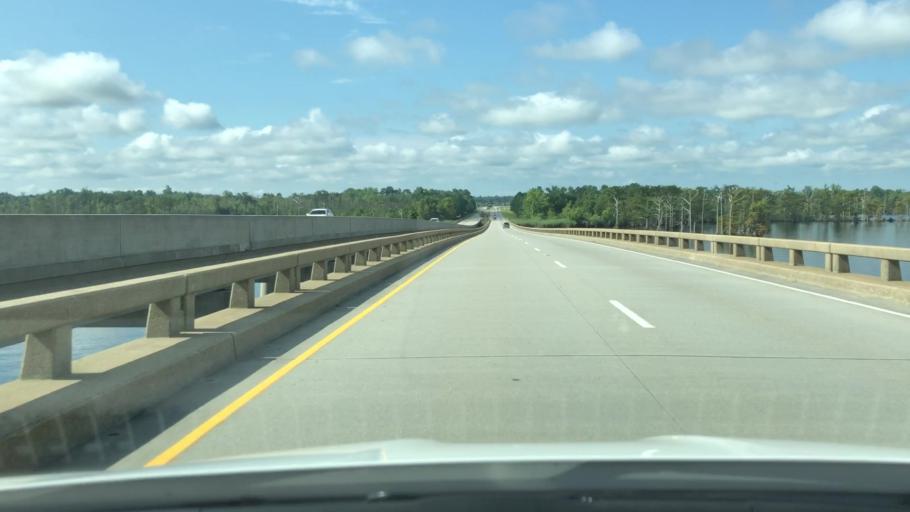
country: US
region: North Carolina
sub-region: Perquimans County
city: Hertford
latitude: 36.1896
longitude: -76.4559
